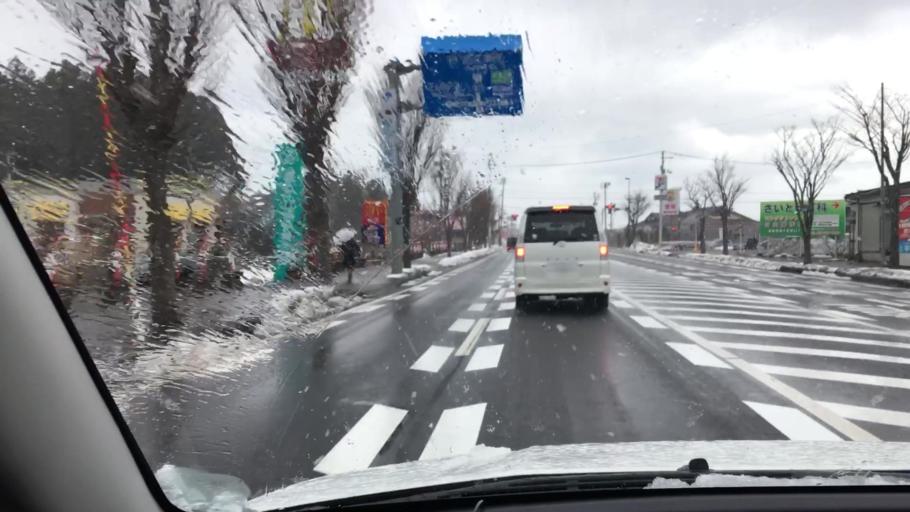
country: JP
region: Niigata
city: Joetsu
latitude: 37.1224
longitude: 138.2324
